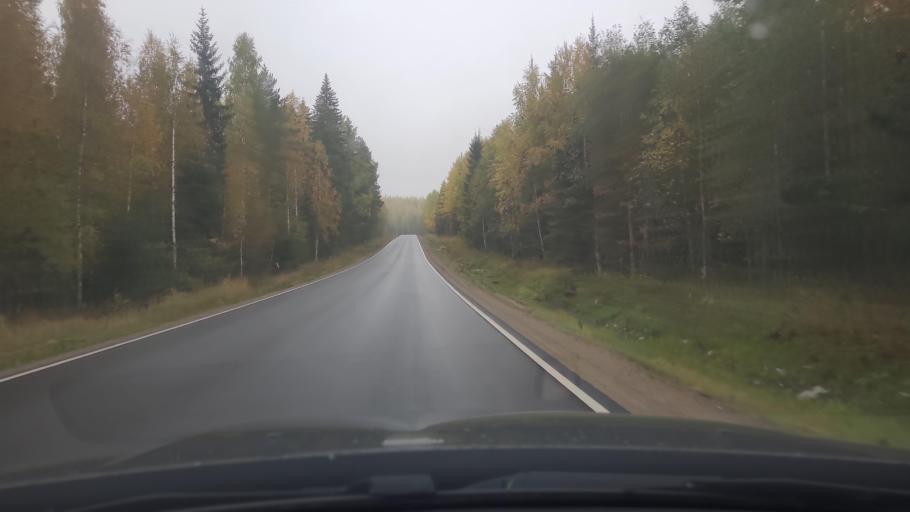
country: FI
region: Northern Savo
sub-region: Varkaus
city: Kangaslampi
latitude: 62.4576
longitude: 28.2683
